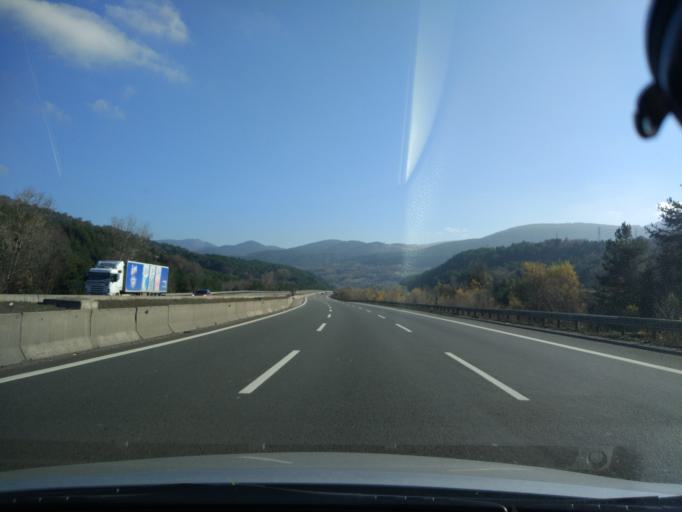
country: TR
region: Bolu
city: Bolu
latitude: 40.7409
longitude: 31.7871
